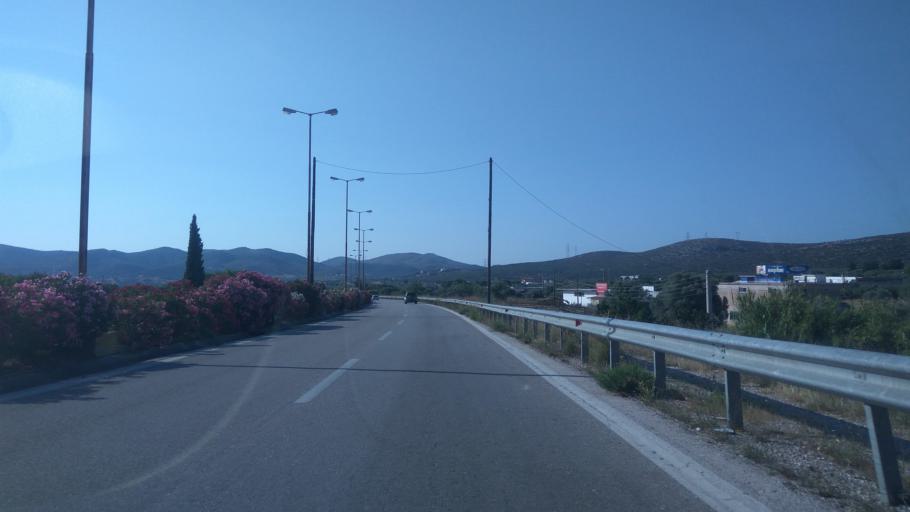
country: GR
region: Attica
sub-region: Nomarchia Anatolikis Attikis
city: Keratea
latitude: 37.8050
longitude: 23.9911
